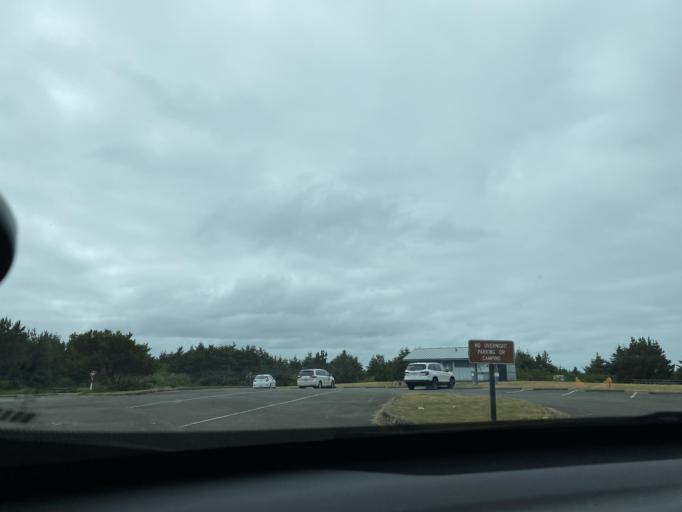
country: US
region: Washington
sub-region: Grays Harbor County
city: Ocean Shores
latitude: 47.1144
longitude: -124.1776
